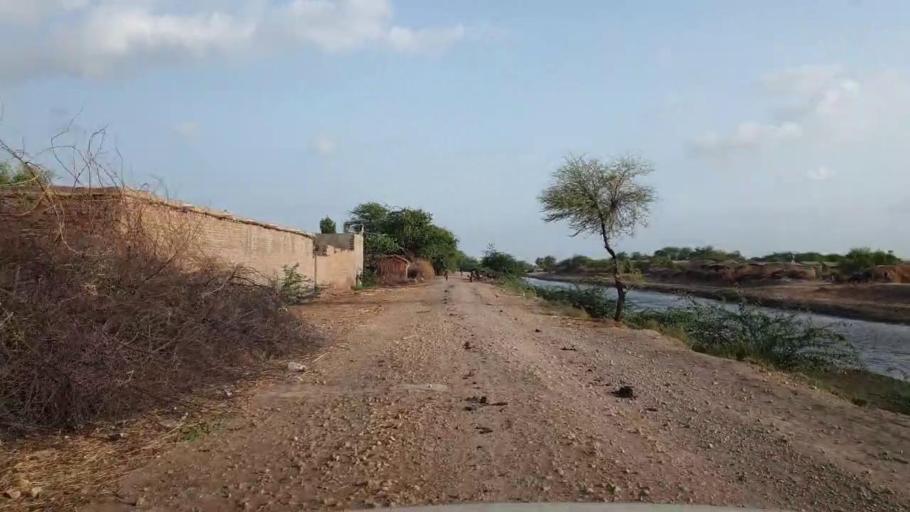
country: PK
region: Sindh
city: Kario
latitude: 24.8013
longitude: 68.6474
